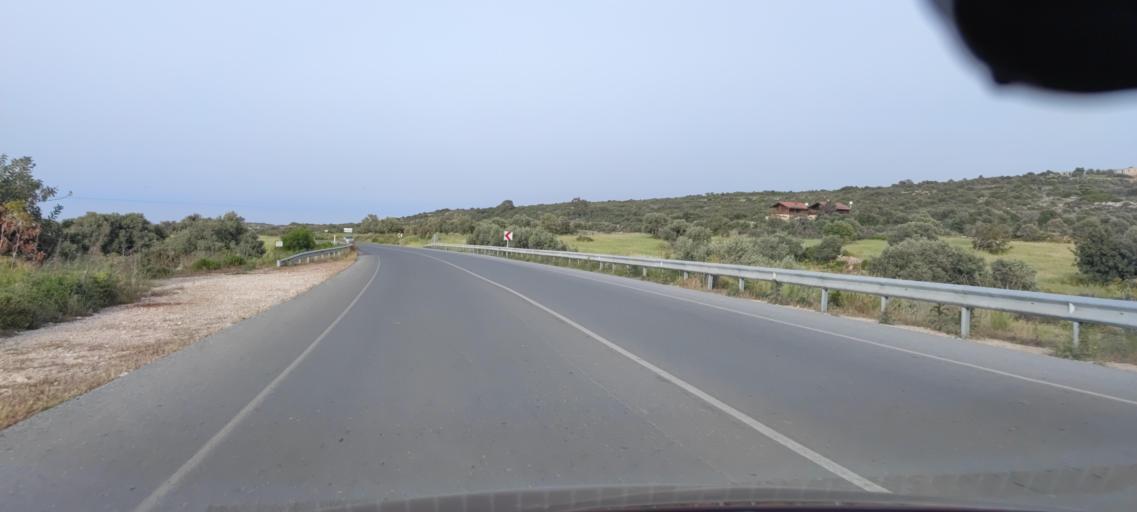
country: CY
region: Ammochostos
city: Leonarisso
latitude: 35.5489
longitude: 34.2060
